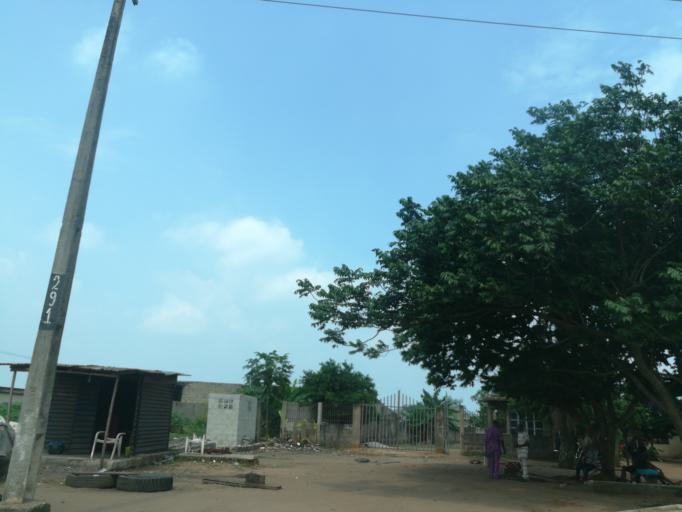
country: NG
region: Lagos
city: Ikorodu
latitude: 6.5993
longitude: 3.6248
